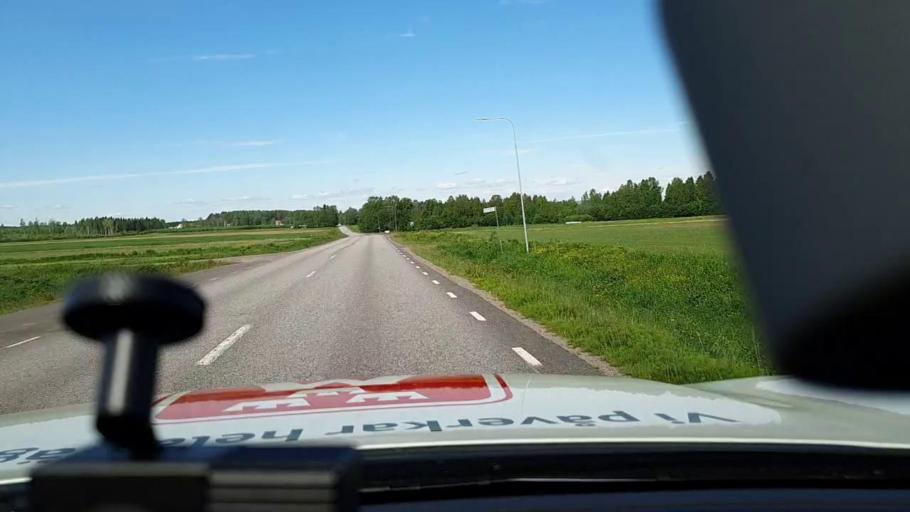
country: SE
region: Norrbotten
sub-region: Lulea Kommun
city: Sodra Sunderbyn
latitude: 65.6515
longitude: 21.8665
